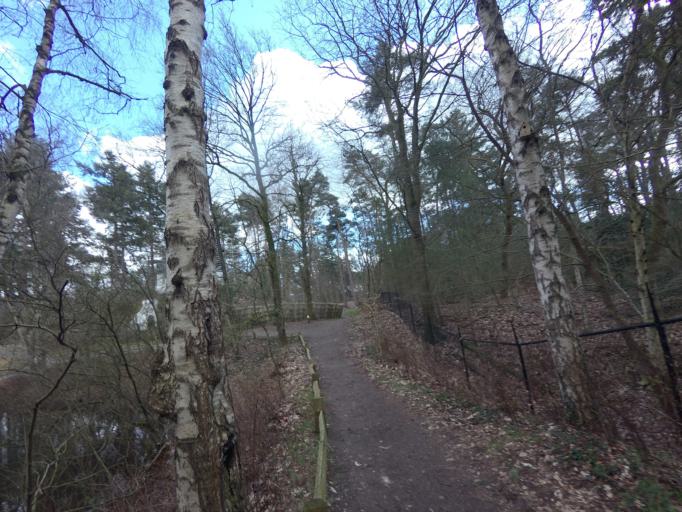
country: NL
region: Utrecht
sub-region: Gemeente Utrechtse Heuvelrug
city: Driebergen-Rijsenburg
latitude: 52.0712
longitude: 5.2717
